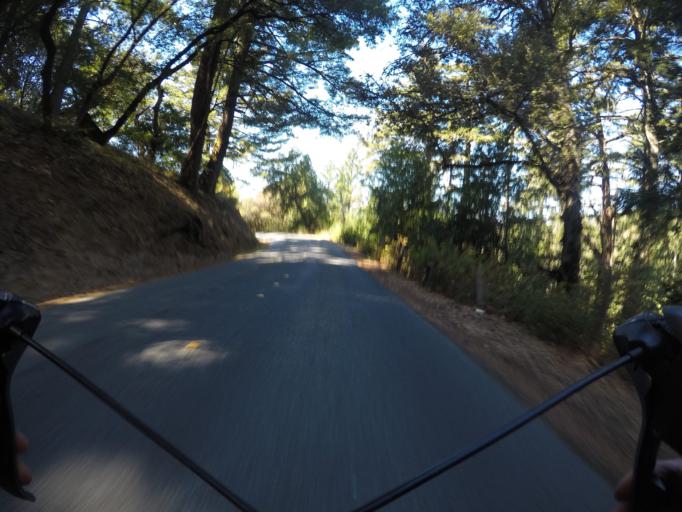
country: US
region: California
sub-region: San Mateo County
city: Portola Valley
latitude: 37.3053
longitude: -122.1990
